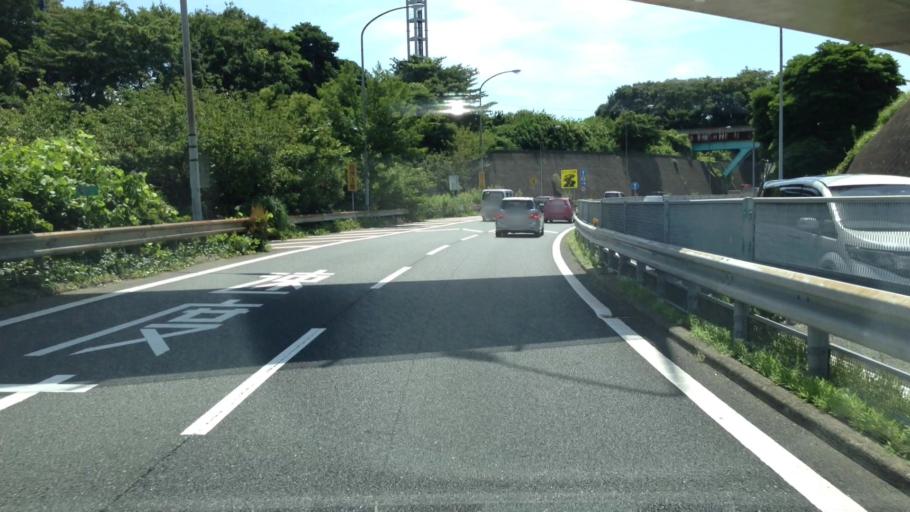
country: JP
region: Kanagawa
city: Yokohama
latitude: 35.4762
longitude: 139.5969
